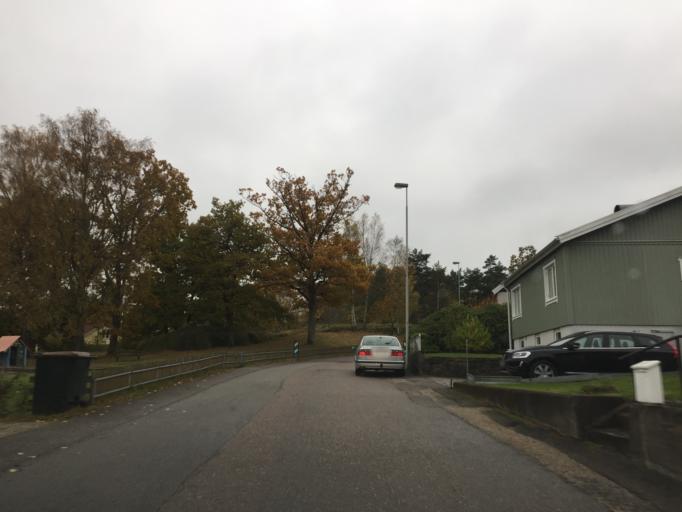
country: SE
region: Vaestra Goetaland
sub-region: Trollhattan
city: Trollhattan
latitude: 58.2882
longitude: 12.2696
